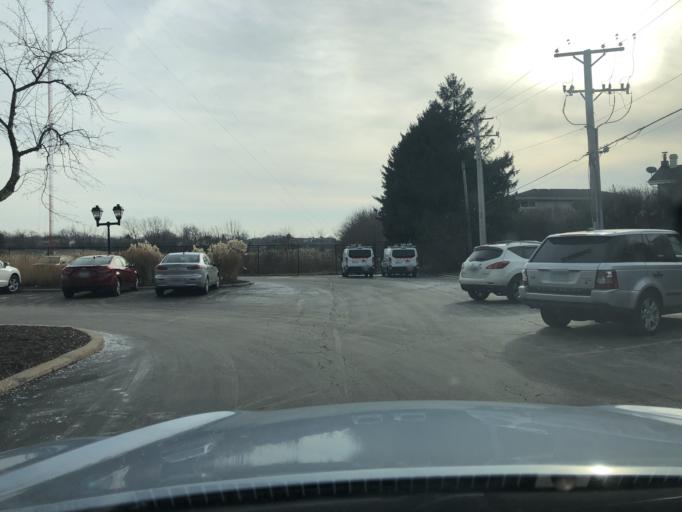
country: US
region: Illinois
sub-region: DuPage County
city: Addison
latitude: 41.9295
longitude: -88.0083
